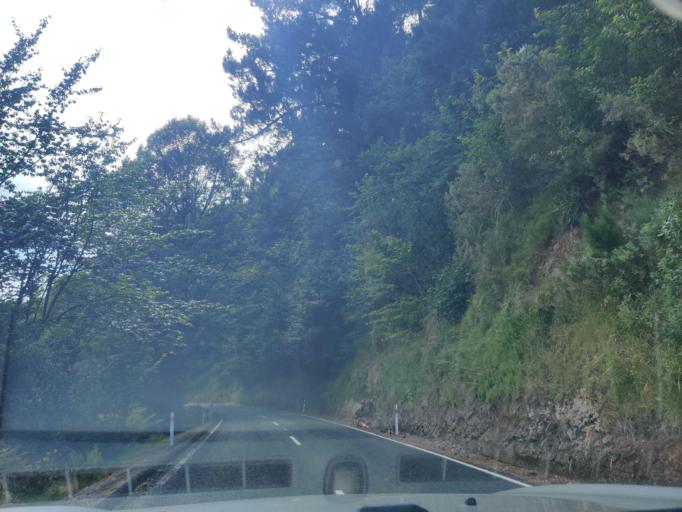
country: NZ
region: Waikato
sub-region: Otorohanga District
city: Otorohanga
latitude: -38.0979
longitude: 175.1221
